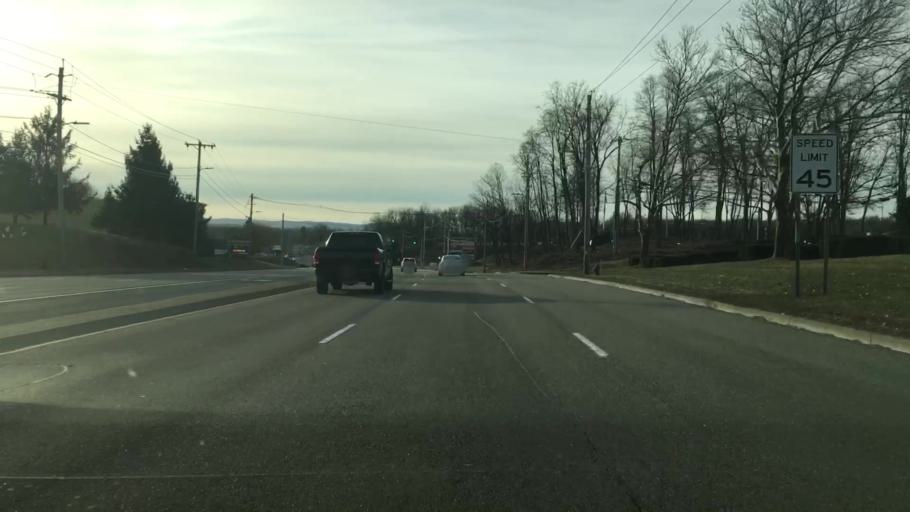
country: US
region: New York
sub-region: Dutchess County
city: Wappingers Falls
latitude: 41.6210
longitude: -73.9174
